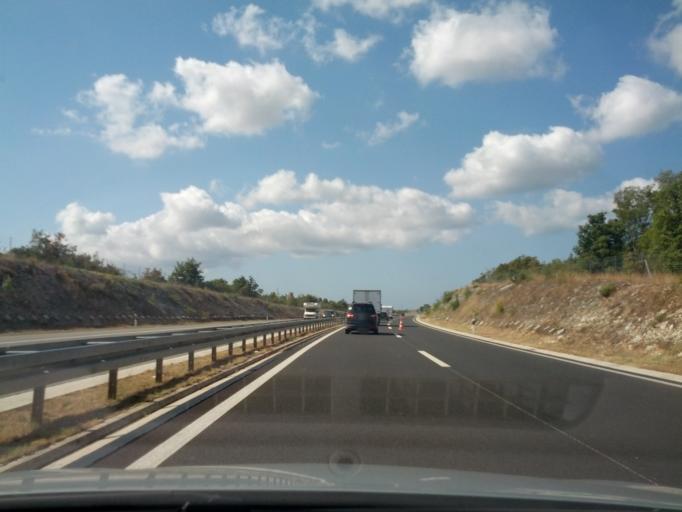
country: HR
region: Istarska
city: Vodnjan
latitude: 45.0173
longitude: 13.8418
